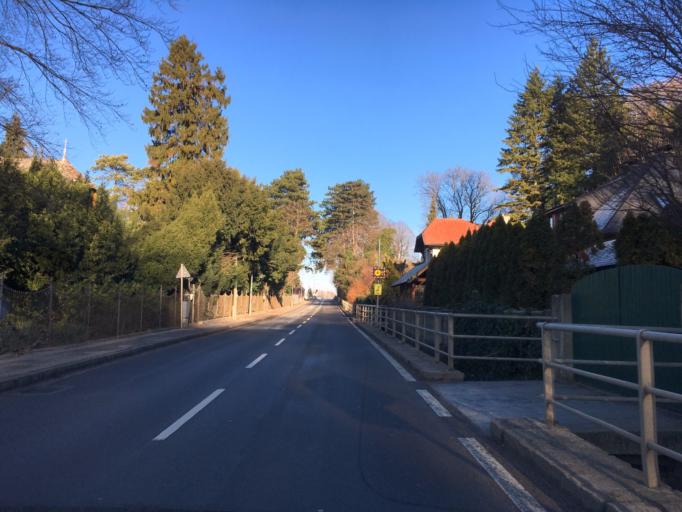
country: AT
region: Lower Austria
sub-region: Politischer Bezirk Tulln
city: Wordern
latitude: 48.3383
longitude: 16.2312
